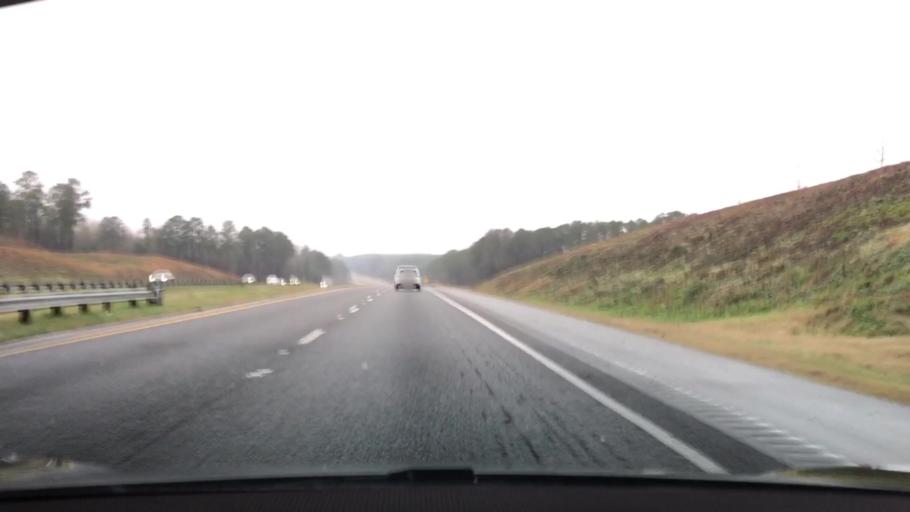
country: US
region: Georgia
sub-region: Walton County
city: Social Circle
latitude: 33.6096
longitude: -83.6995
